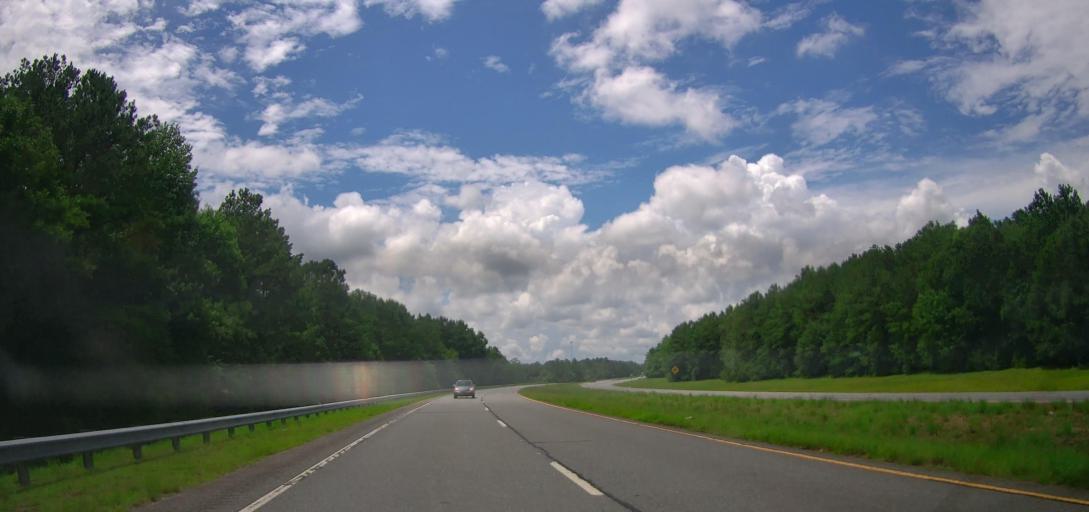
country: US
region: Georgia
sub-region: Dodge County
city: Eastman
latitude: 32.1790
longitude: -83.1892
